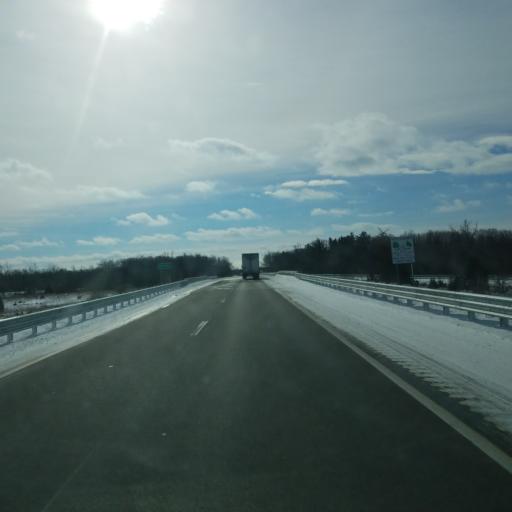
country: US
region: Michigan
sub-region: Gratiot County
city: Ithaca
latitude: 43.3215
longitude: -84.6025
